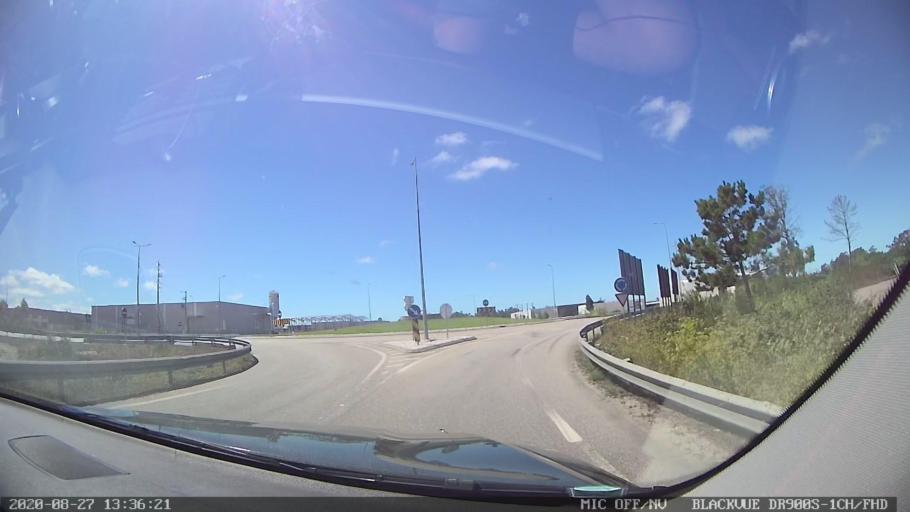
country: PT
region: Coimbra
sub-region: Mira
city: Mira
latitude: 40.4573
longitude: -8.7031
